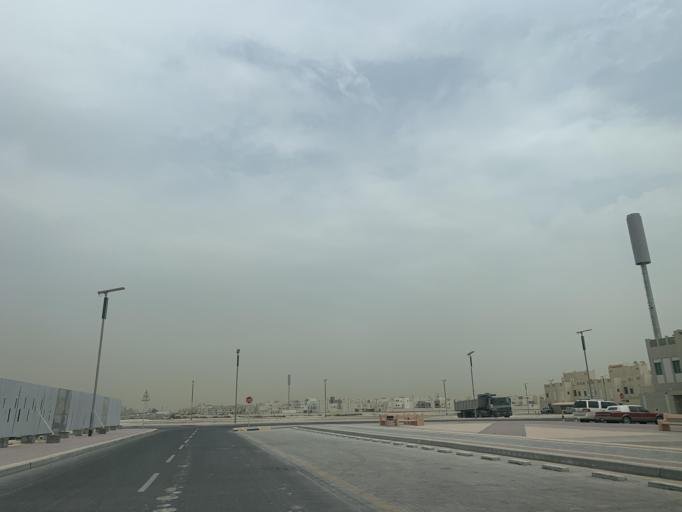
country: BH
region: Northern
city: Madinat `Isa
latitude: 26.1725
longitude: 50.5101
